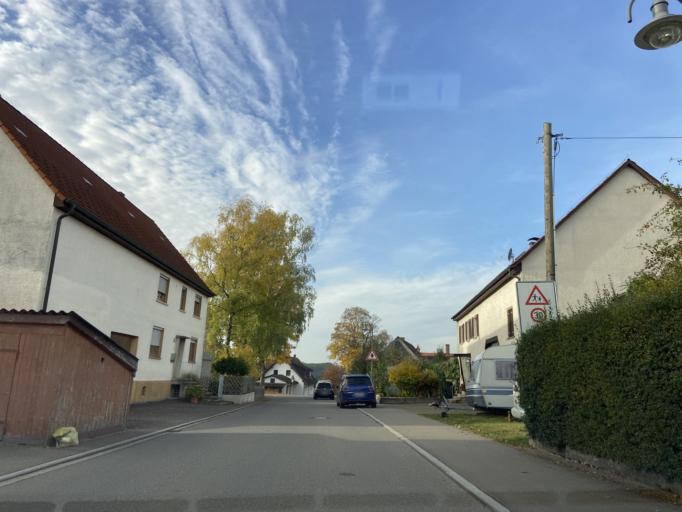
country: DE
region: Baden-Wuerttemberg
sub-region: Tuebingen Region
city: Bingen
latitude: 48.1128
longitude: 9.2753
